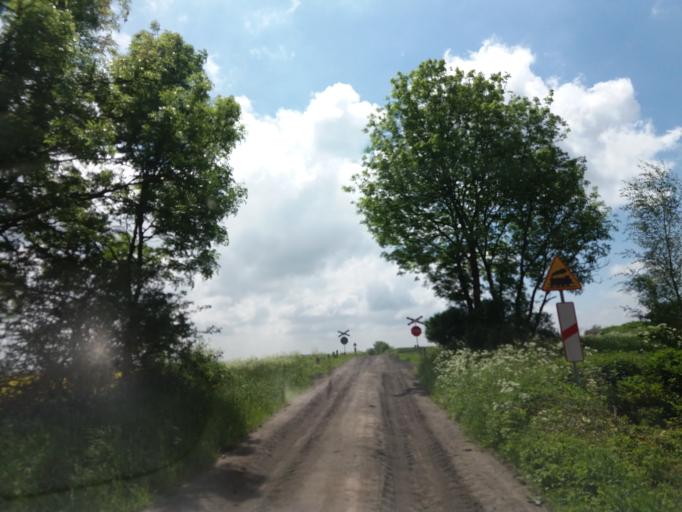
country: PL
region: West Pomeranian Voivodeship
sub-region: Powiat choszczenski
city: Recz
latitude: 53.2824
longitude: 15.5381
